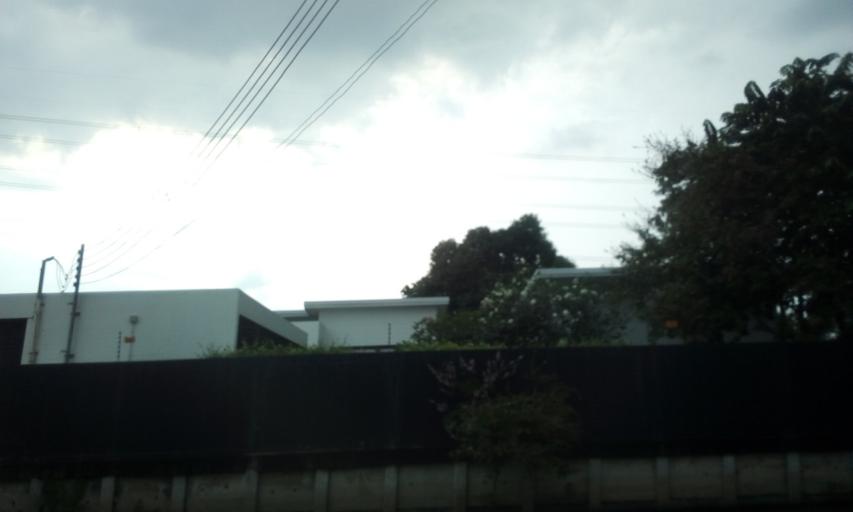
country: TH
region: Bangkok
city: Don Mueang
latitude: 13.9239
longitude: 100.5609
